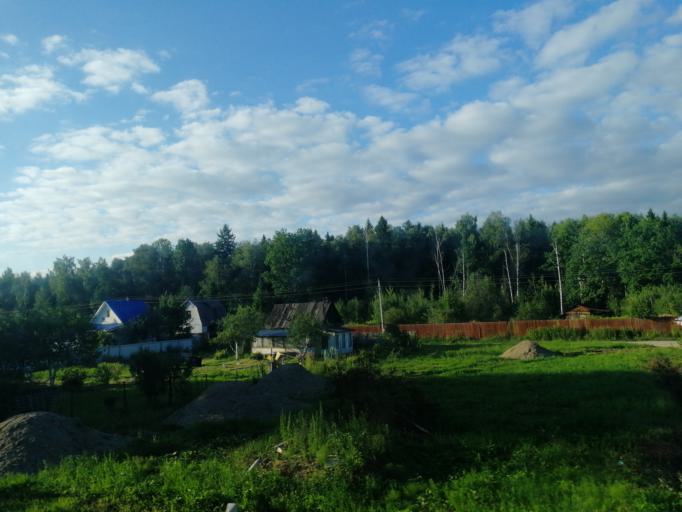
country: RU
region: Kaluga
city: Kaluga
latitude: 54.4519
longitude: 36.2965
